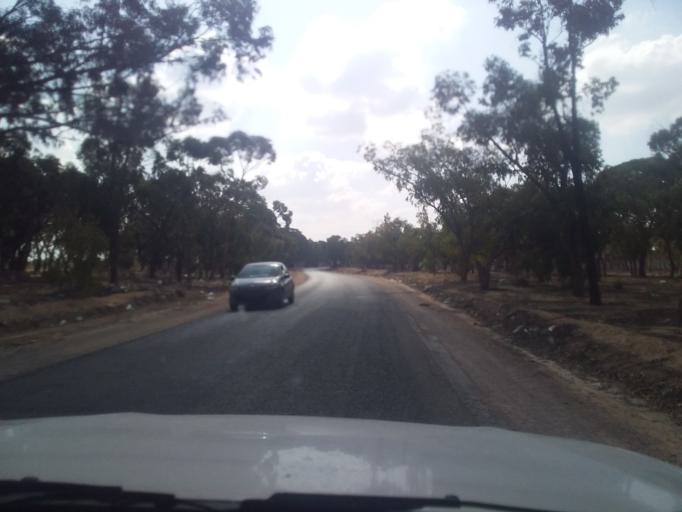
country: TN
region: Qabis
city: Gabes
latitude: 33.6264
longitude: 10.2732
